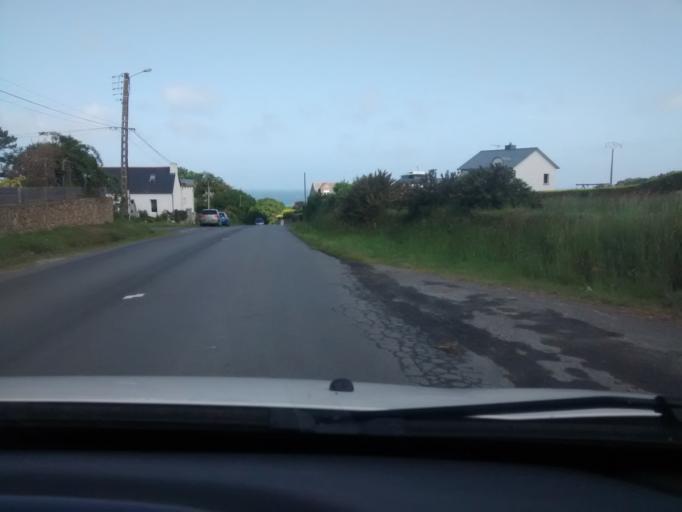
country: FR
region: Brittany
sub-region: Departement des Cotes-d'Armor
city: Trevou-Treguignec
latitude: 48.8176
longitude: -3.3382
